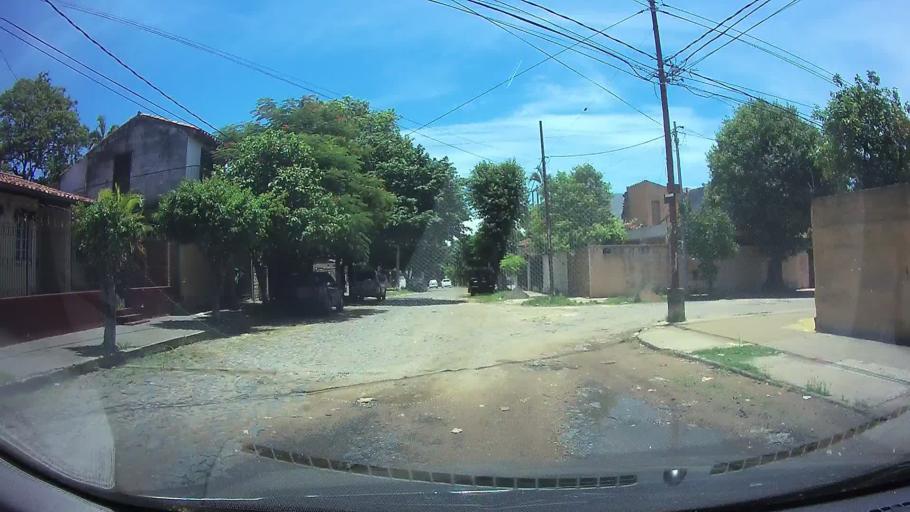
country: PY
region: Asuncion
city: Asuncion
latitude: -25.2708
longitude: -57.5996
